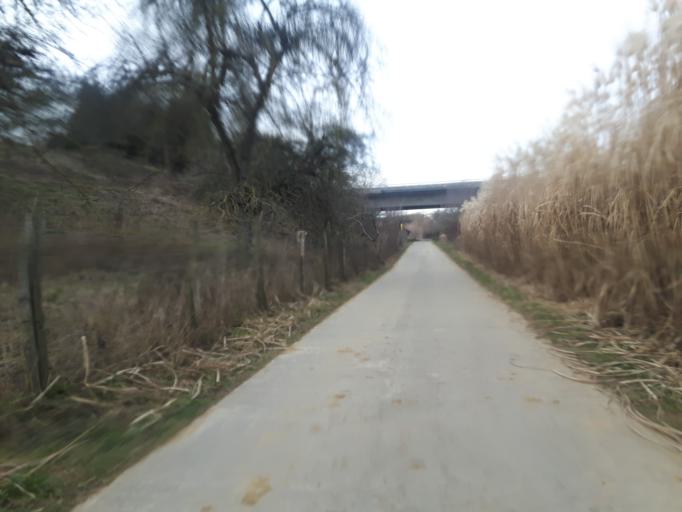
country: DE
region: Baden-Wuerttemberg
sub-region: Regierungsbezirk Stuttgart
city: Bretzfeld
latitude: 49.1945
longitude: 9.4360
